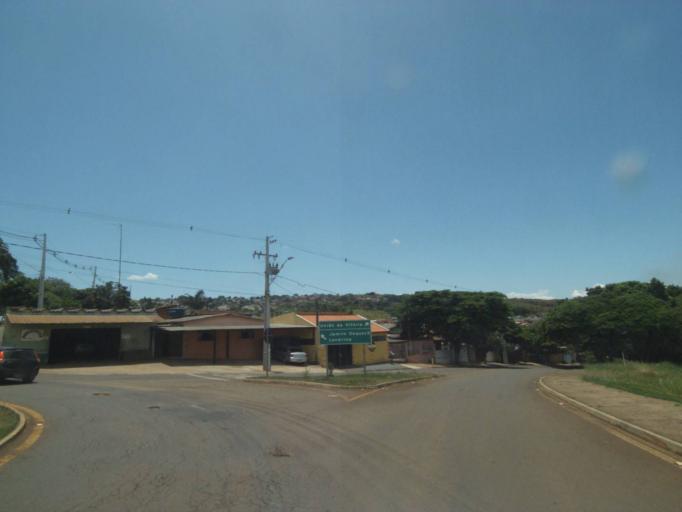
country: BR
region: Parana
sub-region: Londrina
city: Londrina
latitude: -23.3892
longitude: -51.1336
